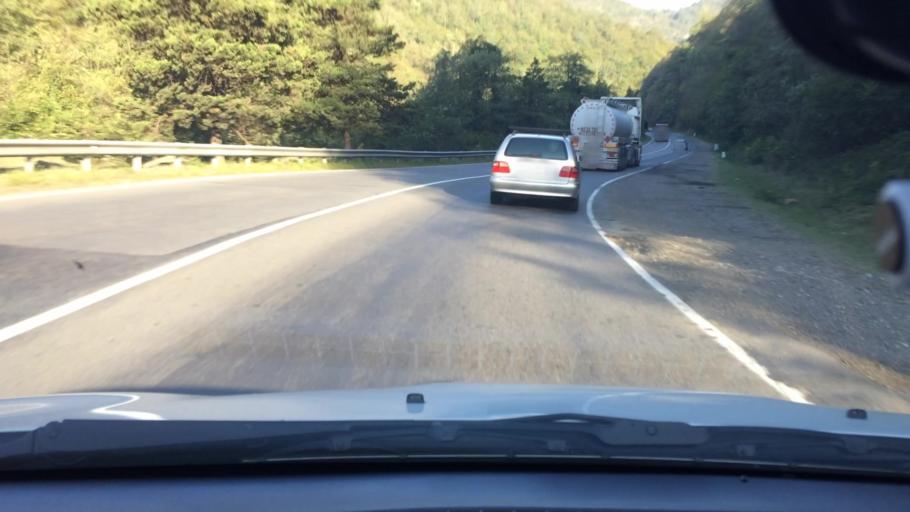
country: GE
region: Imereti
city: Kharagauli
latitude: 42.1045
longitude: 43.2066
